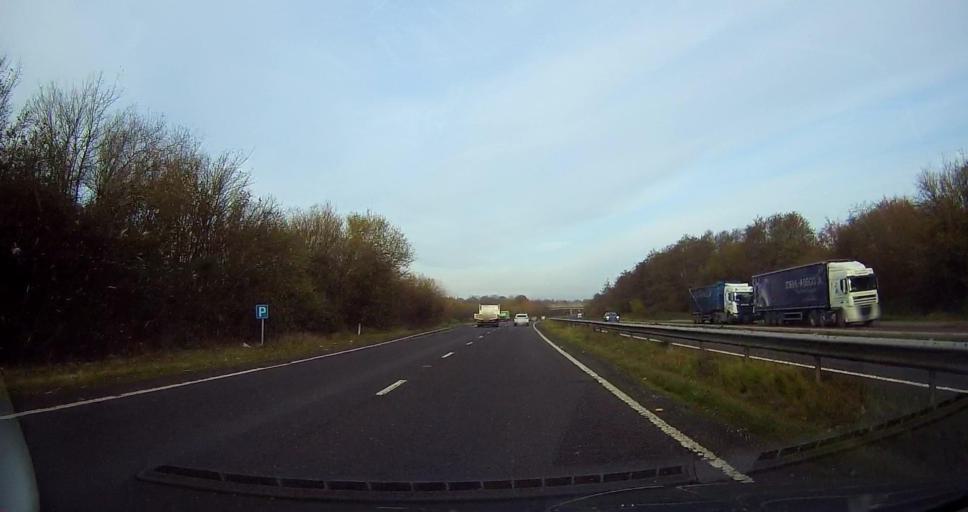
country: GB
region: England
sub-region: West Sussex
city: Hurstpierpoint
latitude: 50.9246
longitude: -0.1945
